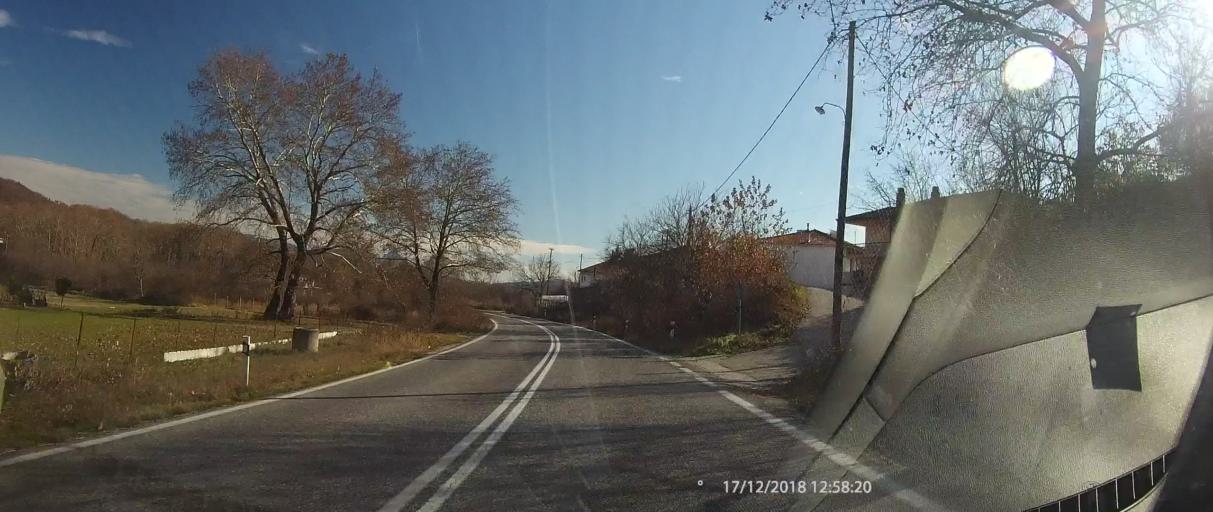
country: GR
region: Thessaly
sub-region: Trikala
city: Kastraki
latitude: 39.7399
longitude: 21.5408
